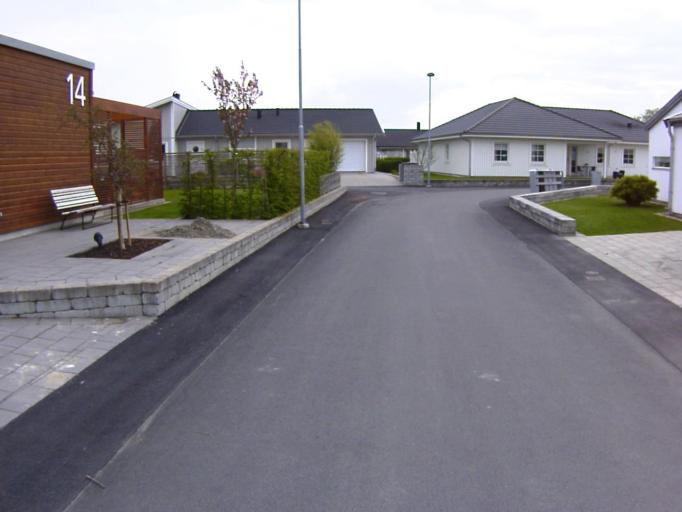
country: SE
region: Skane
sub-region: Kristianstads Kommun
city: Kristianstad
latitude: 56.0178
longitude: 14.1962
